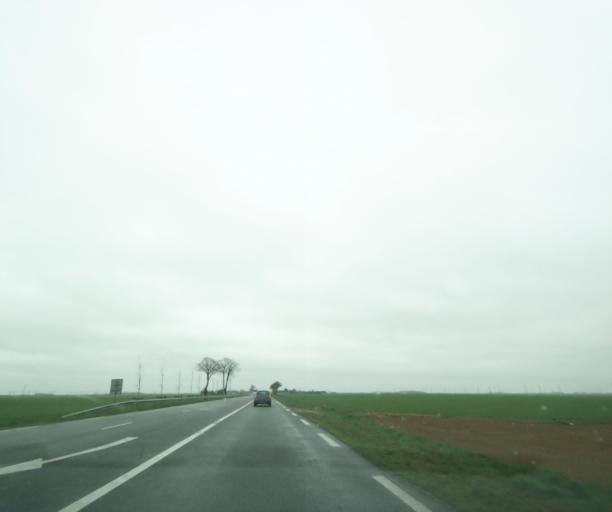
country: FR
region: Centre
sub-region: Departement d'Eure-et-Loir
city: Toury
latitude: 48.2353
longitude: 1.9537
